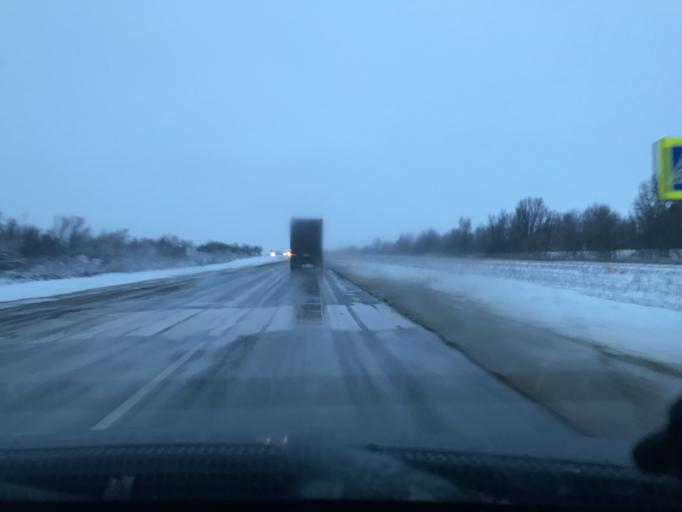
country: RU
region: Rostov
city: Letnik
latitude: 46.0158
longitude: 41.2112
